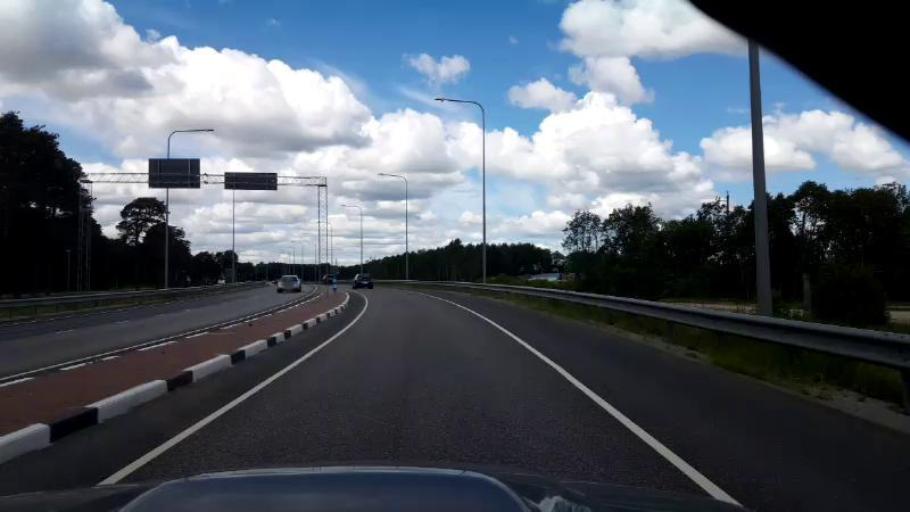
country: EE
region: Paernumaa
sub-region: Paikuse vald
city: Paikuse
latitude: 58.3624
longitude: 24.5650
